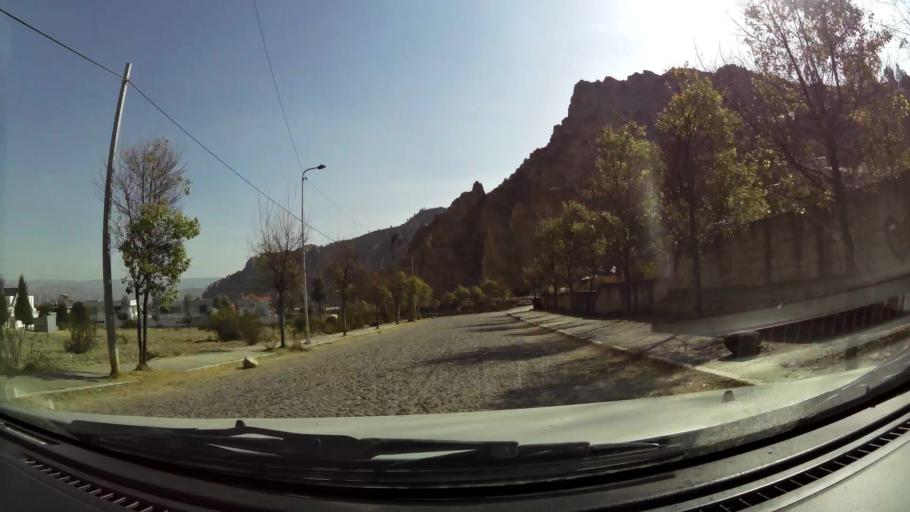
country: BO
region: La Paz
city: La Paz
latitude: -16.5119
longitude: -68.0583
